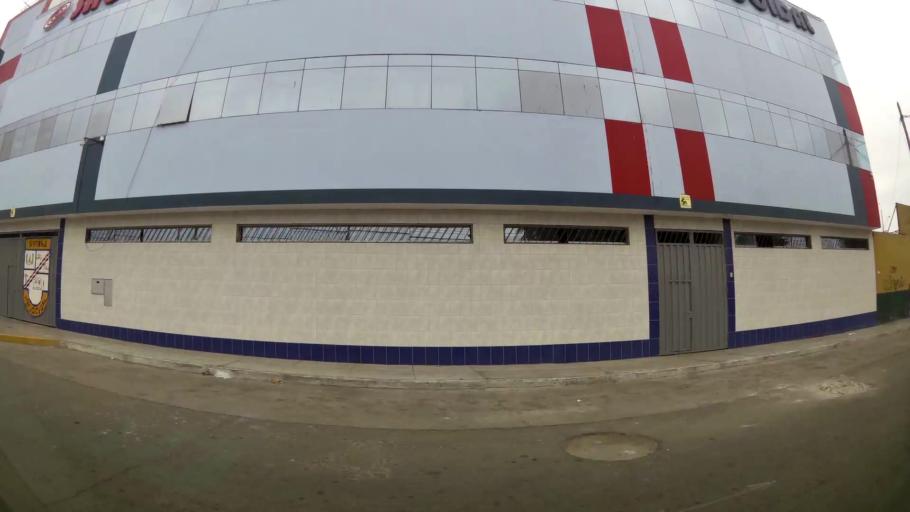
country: PE
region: Callao
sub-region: Callao
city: Callao
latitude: -12.0594
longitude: -77.1257
